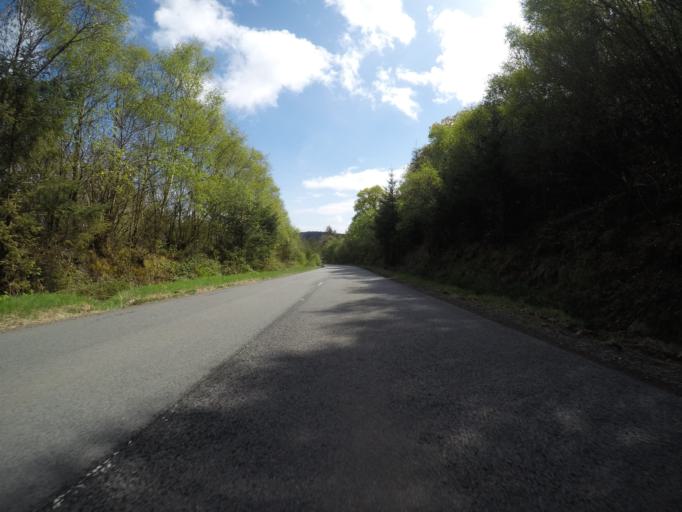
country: GB
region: Scotland
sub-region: Highland
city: Isle of Skye
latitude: 57.4596
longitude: -6.3289
